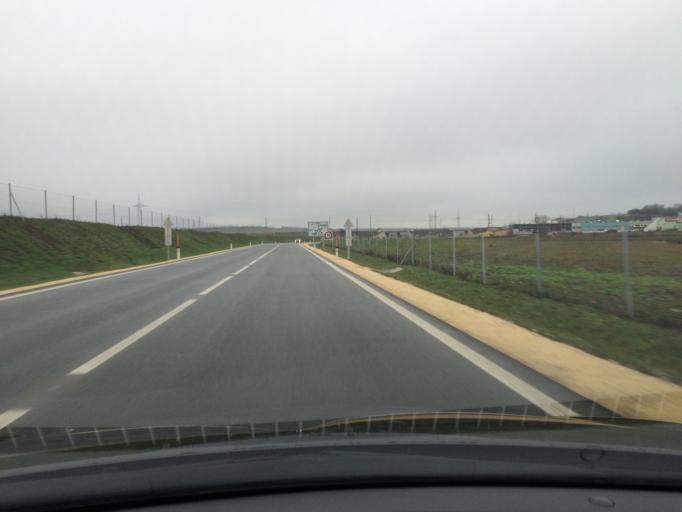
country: AT
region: Lower Austria
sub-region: Politischer Bezirk Mistelbach
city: Mistelbach
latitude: 48.5585
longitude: 16.5567
